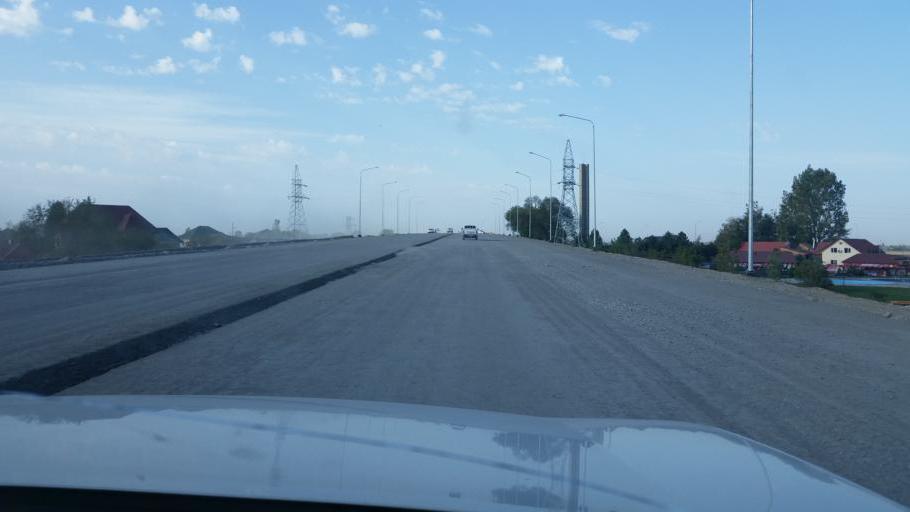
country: KZ
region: Almaty Oblysy
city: Energeticheskiy
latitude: 43.4425
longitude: 76.9921
